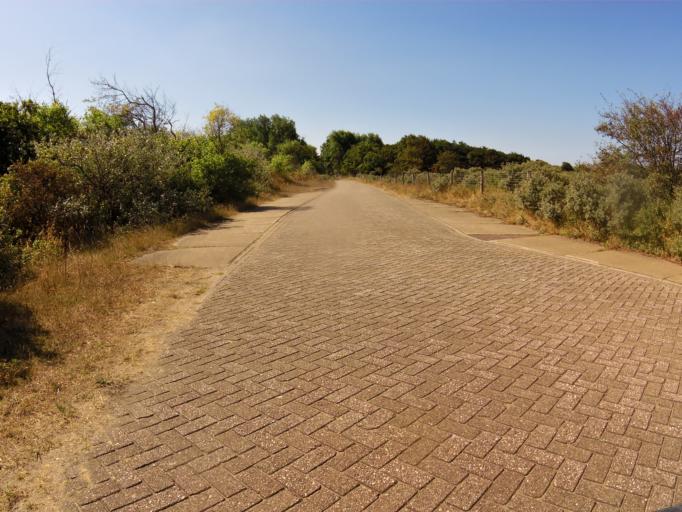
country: NL
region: North Holland
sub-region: Gemeente Beverwijk
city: Beverwijk
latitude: 52.4999
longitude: 4.6016
